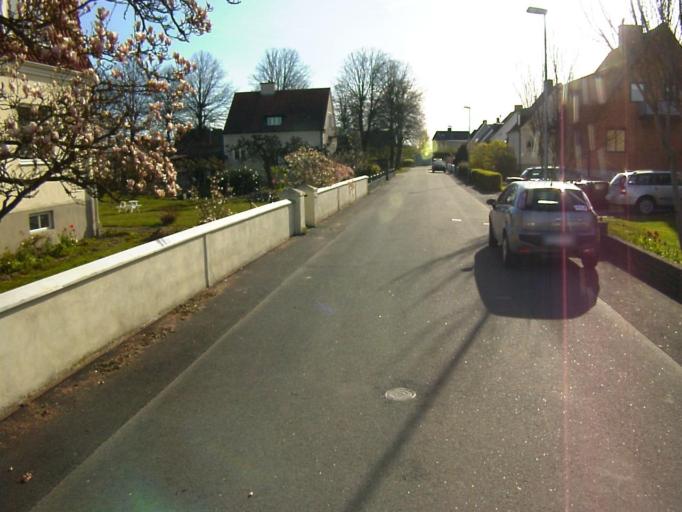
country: SE
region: Skane
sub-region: Kristianstads Kommun
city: Kristianstad
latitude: 56.0151
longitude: 14.1477
